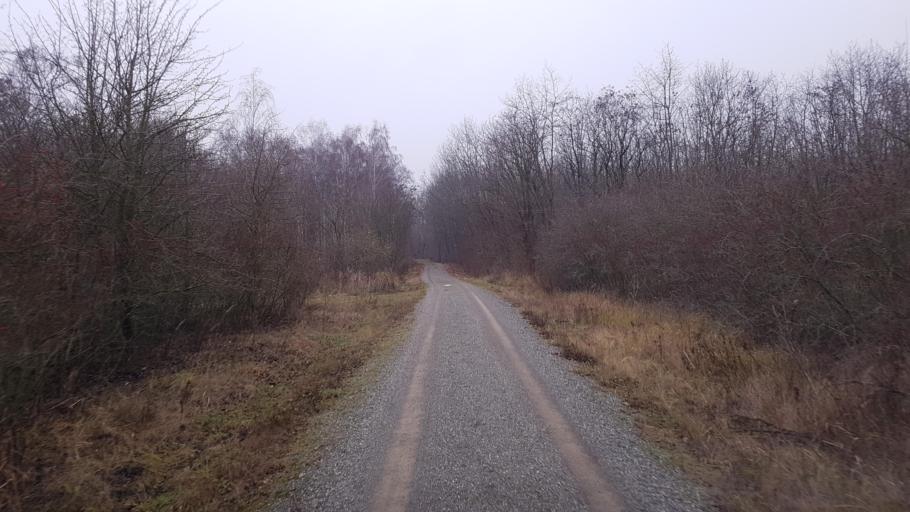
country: DE
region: Brandenburg
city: Plessa
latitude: 51.4886
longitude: 13.6385
